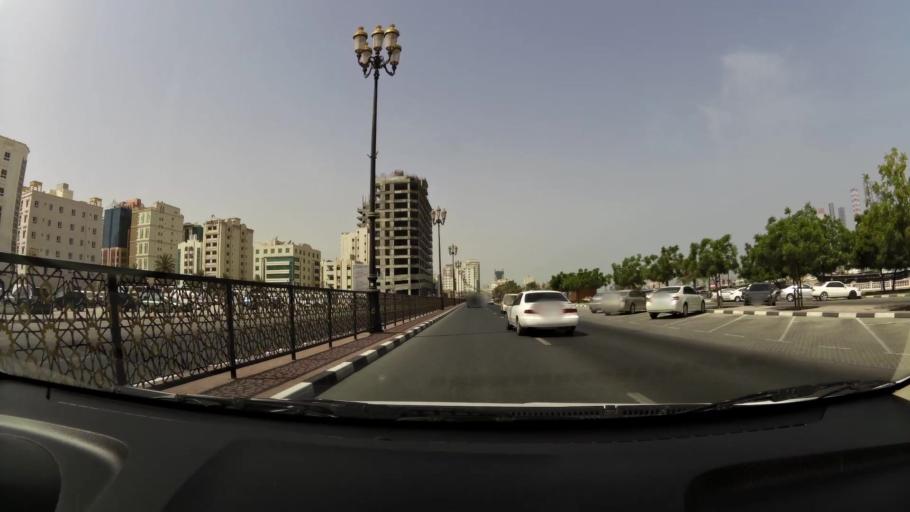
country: AE
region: Ash Shariqah
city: Sharjah
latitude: 25.3682
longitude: 55.3911
